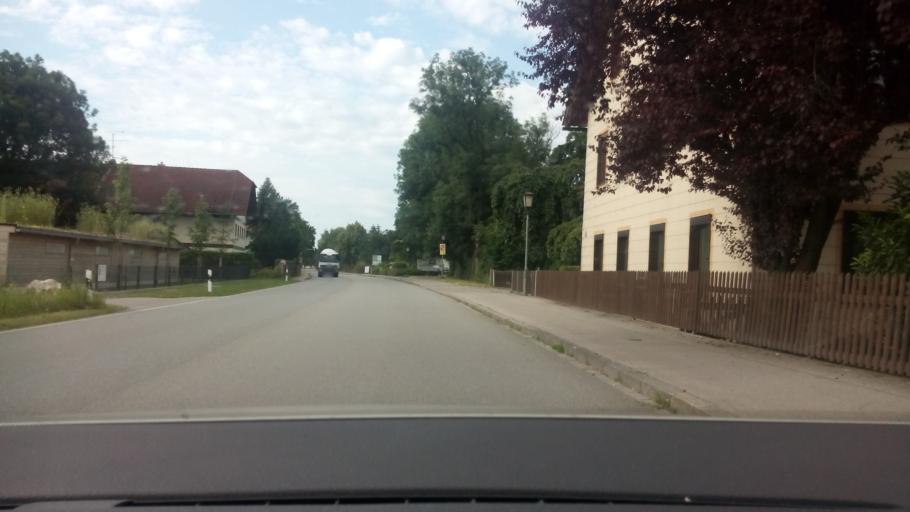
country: DE
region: Bavaria
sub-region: Upper Bavaria
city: Garching bei Munchen
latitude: 48.2338
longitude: 11.6413
